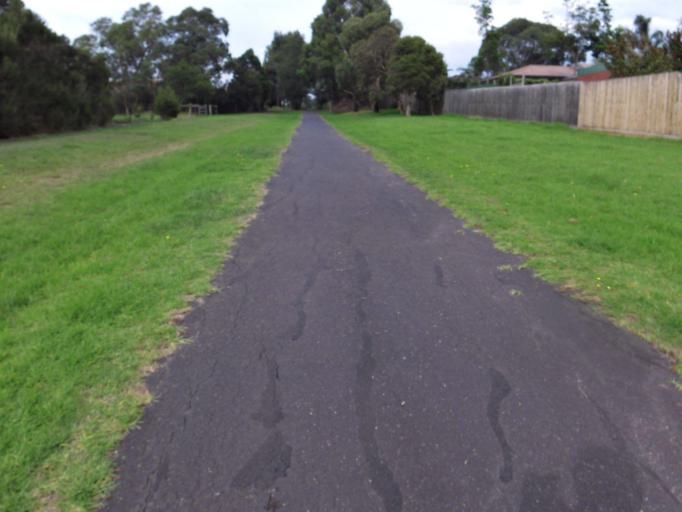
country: AU
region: Victoria
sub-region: Casey
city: Berwick
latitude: -38.0187
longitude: 145.3275
